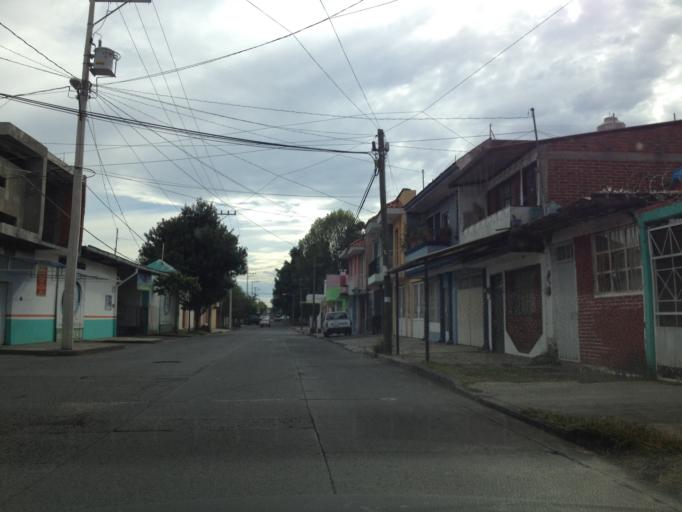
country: MX
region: Michoacan
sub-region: Uruapan
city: Uruapan
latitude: 19.4078
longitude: -102.0418
